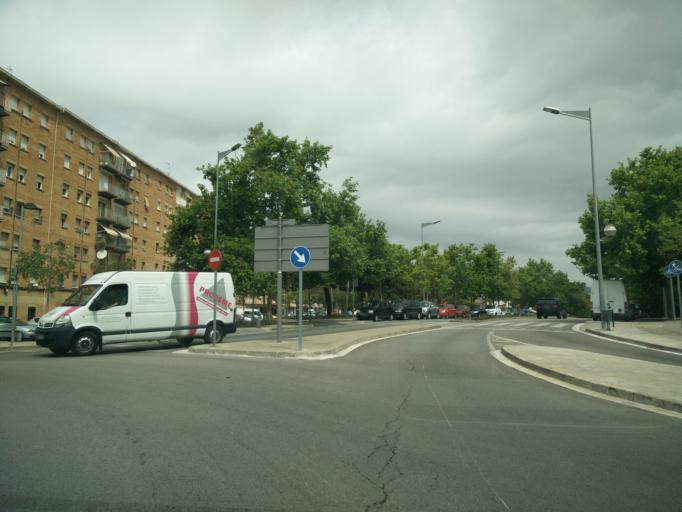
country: ES
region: Catalonia
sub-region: Provincia de Barcelona
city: Terrassa
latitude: 41.5521
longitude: 2.0263
